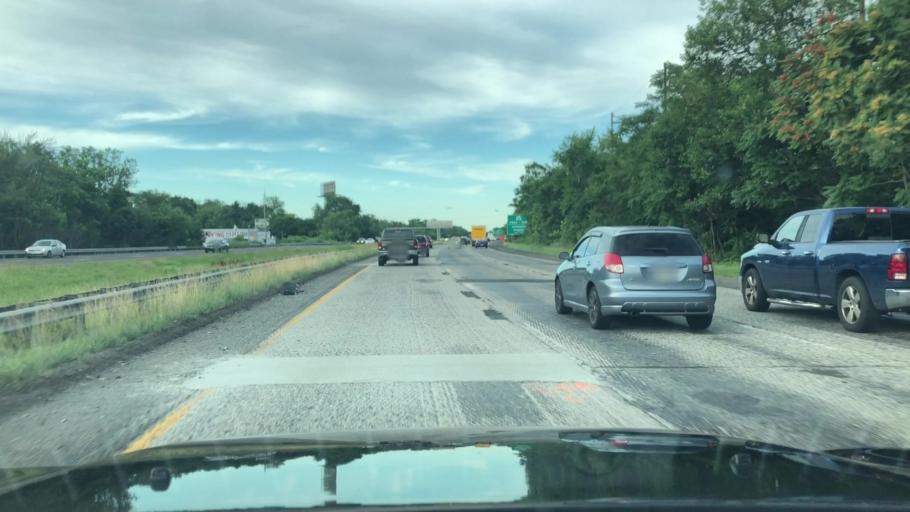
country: US
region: New Jersey
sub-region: Burlington County
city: Delanco
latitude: 40.0592
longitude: -74.9802
